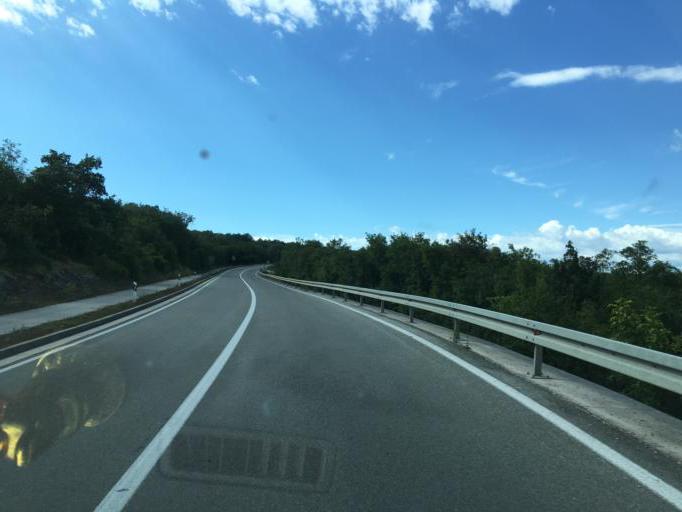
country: HR
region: Primorsko-Goranska
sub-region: Grad Krk
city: Krk
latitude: 45.0778
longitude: 14.5464
